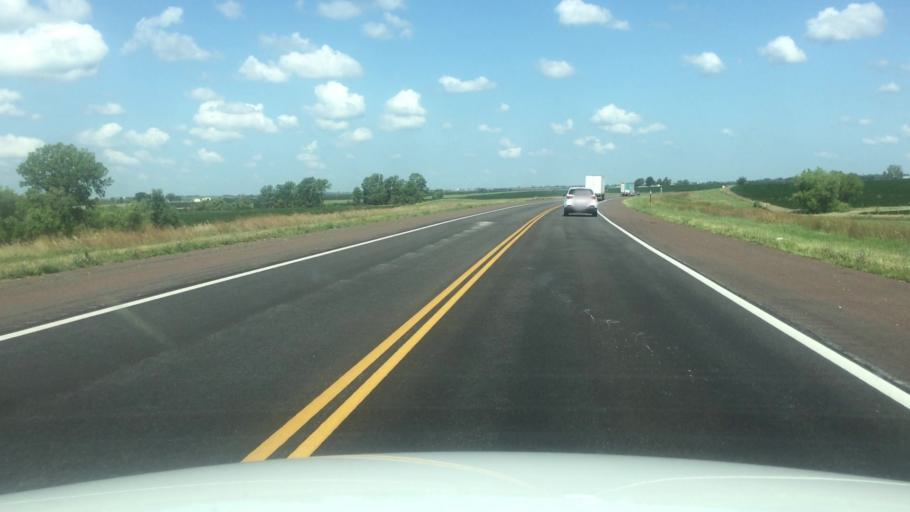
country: US
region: Kansas
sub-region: Nemaha County
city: Sabetha
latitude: 39.8673
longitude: -95.7738
